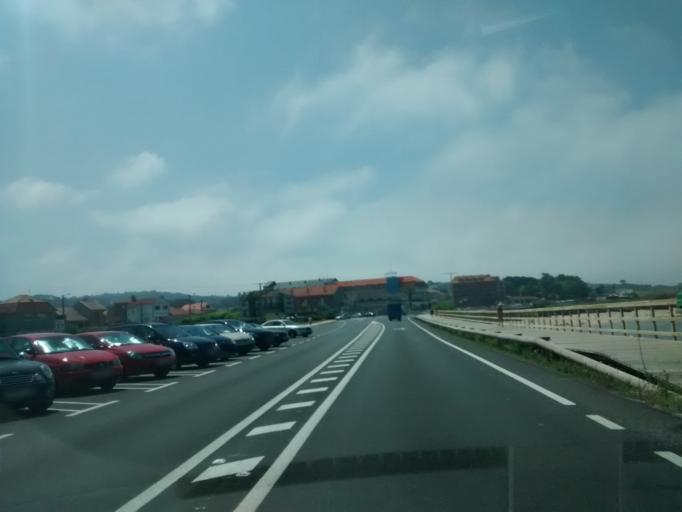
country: ES
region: Galicia
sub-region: Provincia de Pontevedra
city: O Grove
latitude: 42.4359
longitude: -8.8706
